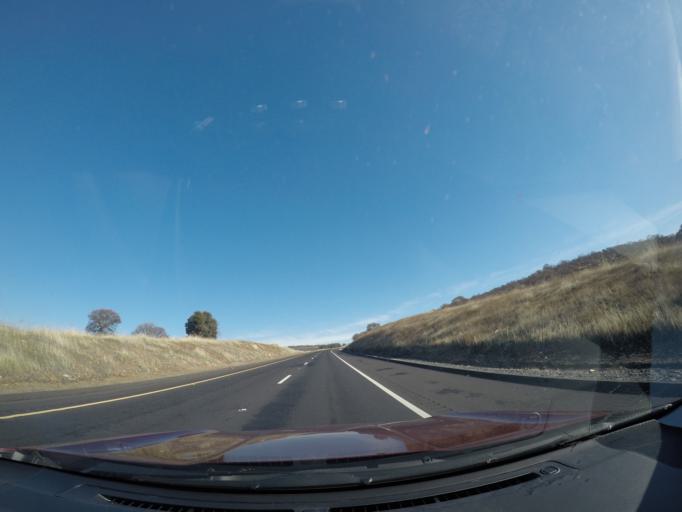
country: US
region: California
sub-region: Calaveras County
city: Copperopolis
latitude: 37.8432
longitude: -120.6183
